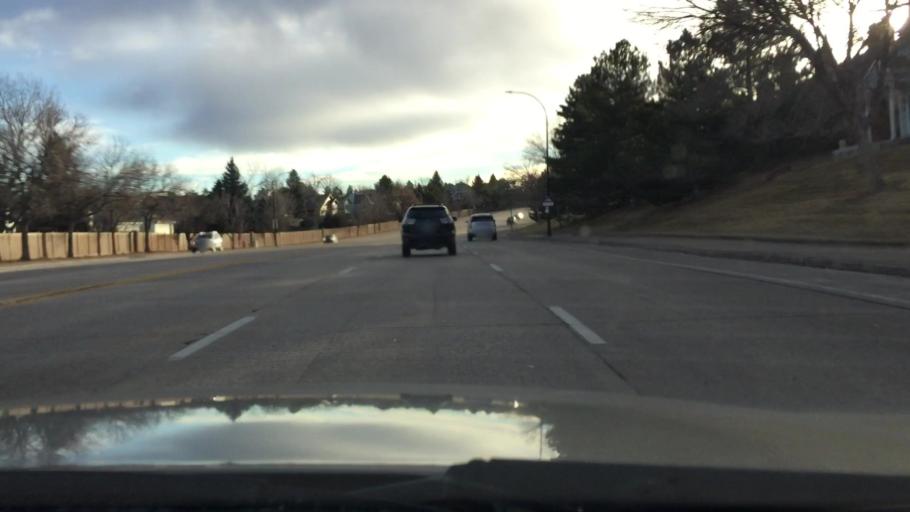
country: US
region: Colorado
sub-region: Douglas County
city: Highlands Ranch
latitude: 39.5462
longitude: -104.9790
